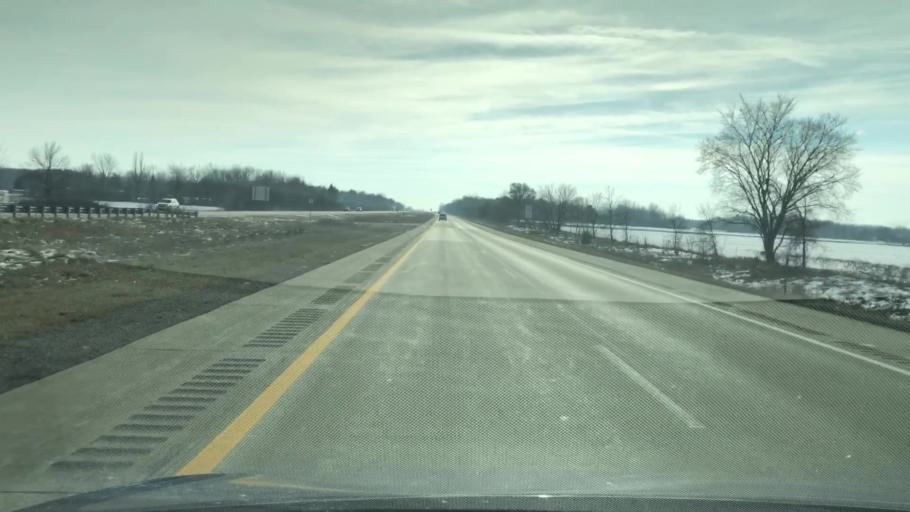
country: US
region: Michigan
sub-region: Bay County
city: Pinconning
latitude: 43.8434
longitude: -84.0217
